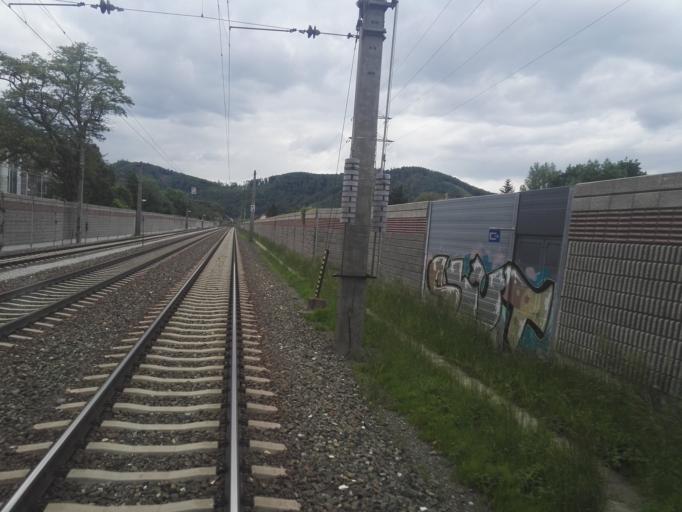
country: AT
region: Styria
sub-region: Graz Stadt
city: Goesting
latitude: 47.0990
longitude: 15.4003
